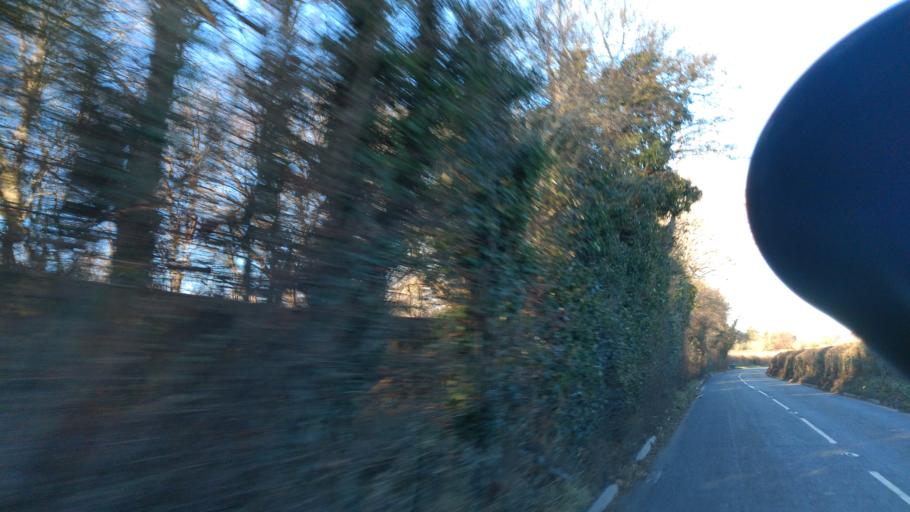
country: GB
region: England
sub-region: Wiltshire
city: Westwood
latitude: 51.3263
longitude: -2.2582
